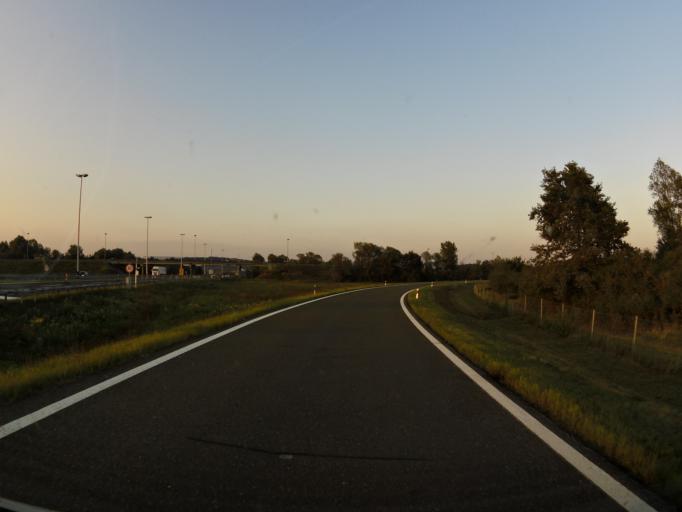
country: HR
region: Zagrebacka
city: Jakovlje
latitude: 45.9972
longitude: 15.8636
